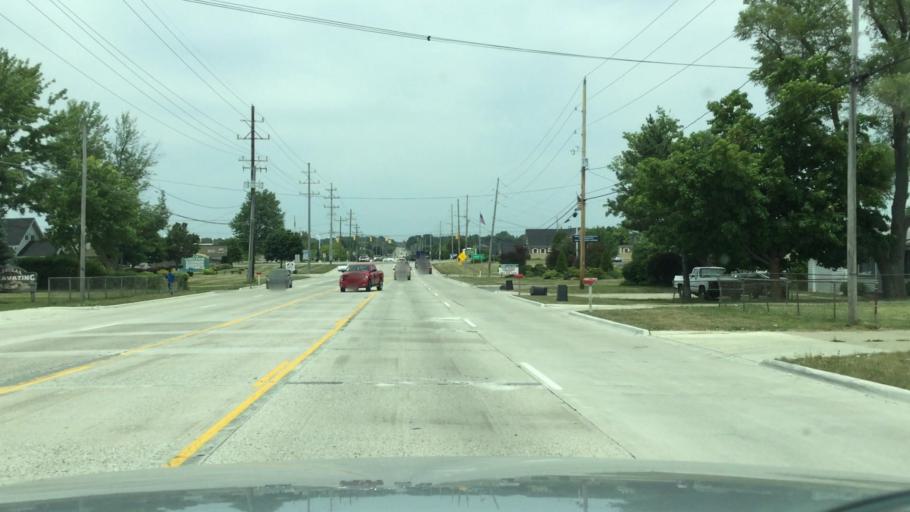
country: US
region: Michigan
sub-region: Genesee County
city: Swartz Creek
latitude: 43.0047
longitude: -83.7727
